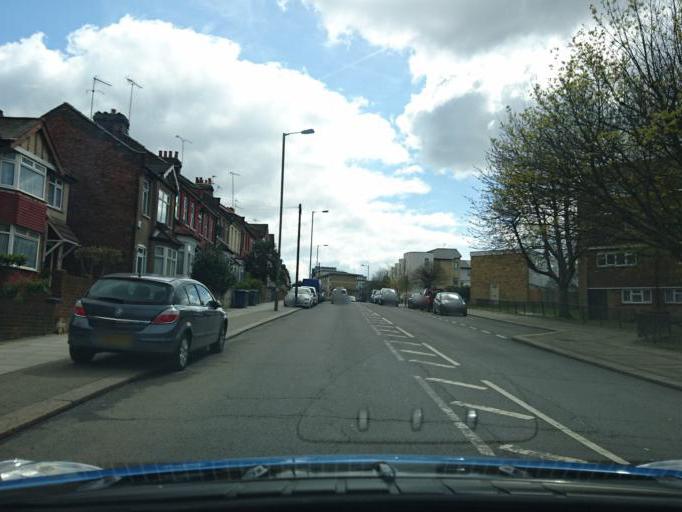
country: GB
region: England
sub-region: Greater London
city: Wood Green
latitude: 51.6186
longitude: -0.1444
